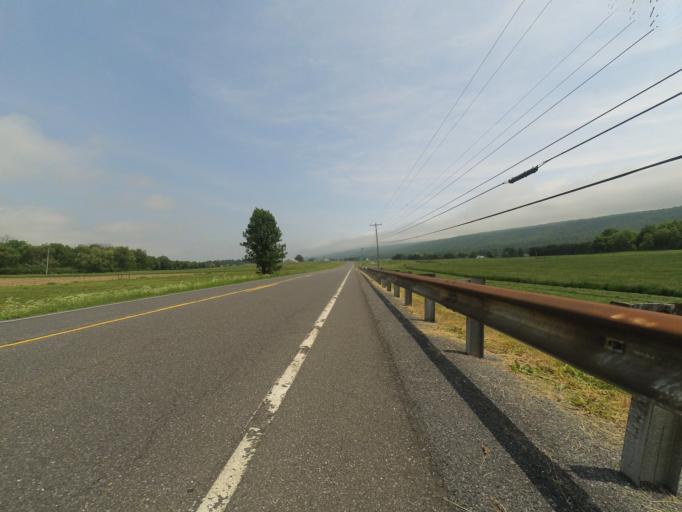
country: US
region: Pennsylvania
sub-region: Centre County
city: Pine Grove Mills
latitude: 40.7123
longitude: -77.9587
